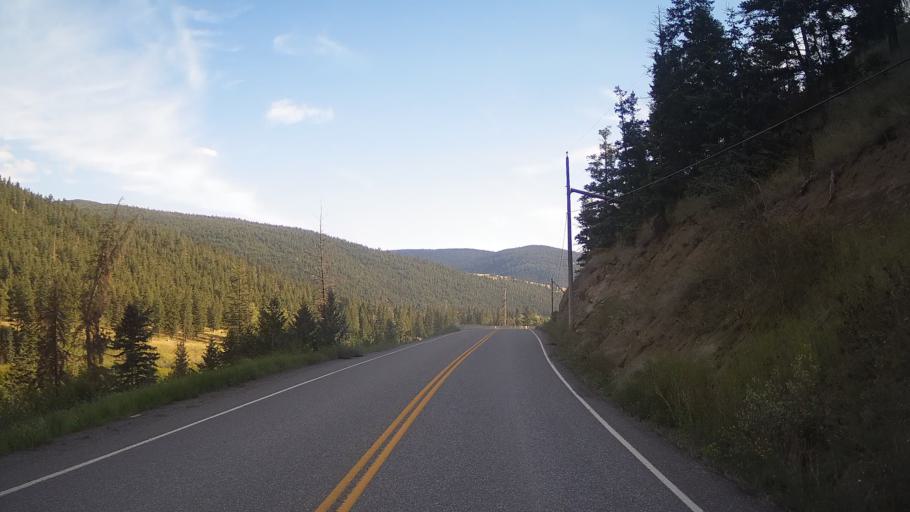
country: CA
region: British Columbia
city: Cache Creek
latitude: 50.8581
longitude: -121.5311
